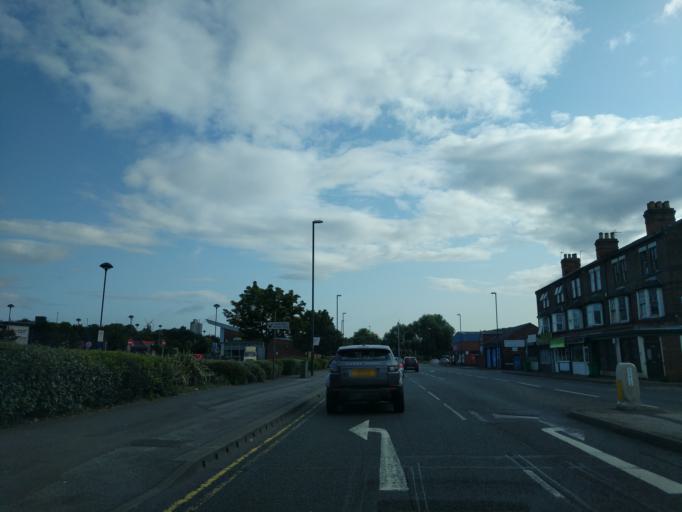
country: GB
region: England
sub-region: Nottinghamshire
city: West Bridgford
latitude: 52.9452
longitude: -1.1320
